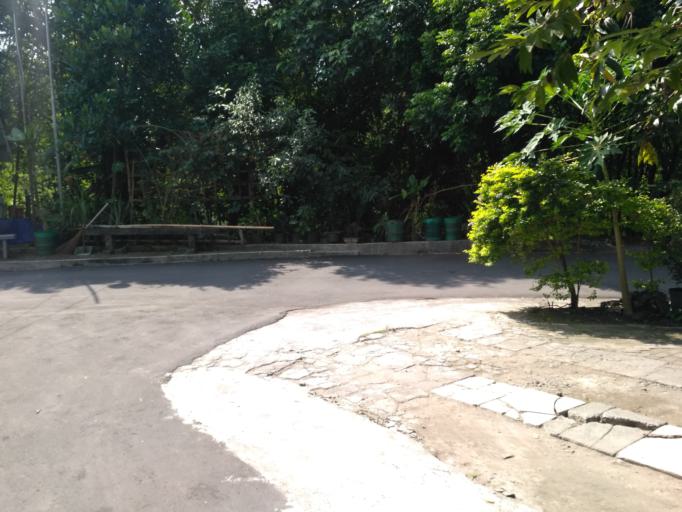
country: ID
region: Daerah Istimewa Yogyakarta
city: Depok
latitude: -7.7445
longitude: 110.4147
